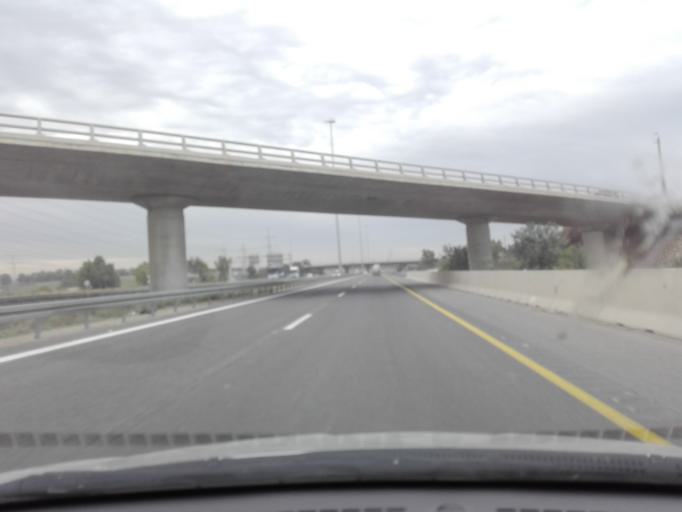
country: IL
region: Central District
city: Ramla
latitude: 31.9092
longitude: 34.8947
